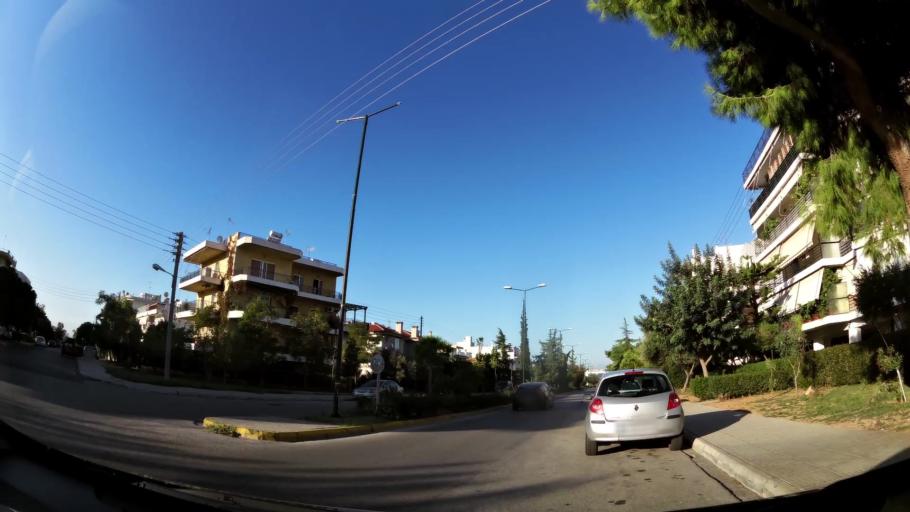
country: GR
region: Attica
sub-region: Nomarchia Athinas
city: Glyfada
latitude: 37.8846
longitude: 23.7562
